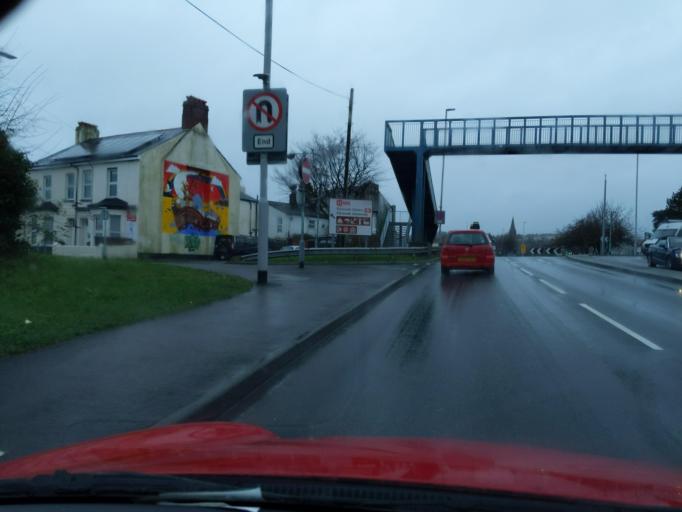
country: GB
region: England
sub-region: Plymouth
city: Plymouth
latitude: 50.3693
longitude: -4.1250
